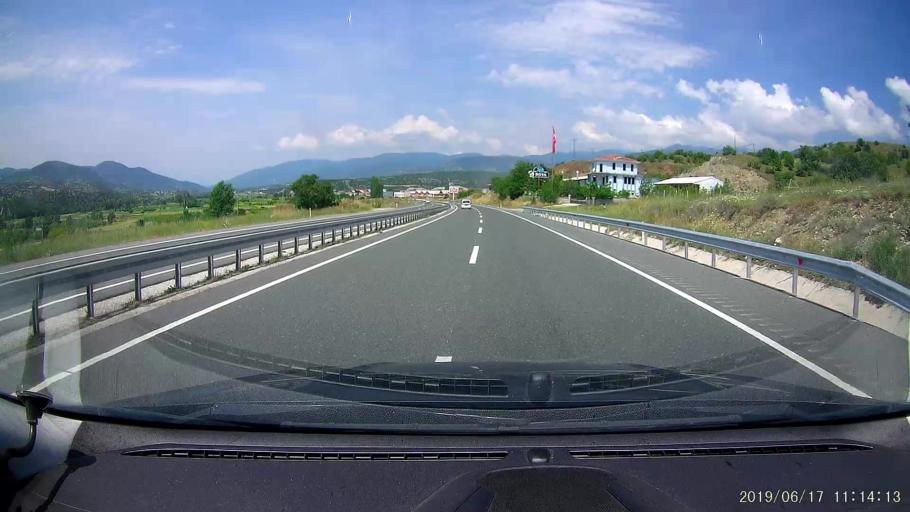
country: TR
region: Kastamonu
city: Tosya
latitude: 40.9572
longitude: 33.9542
